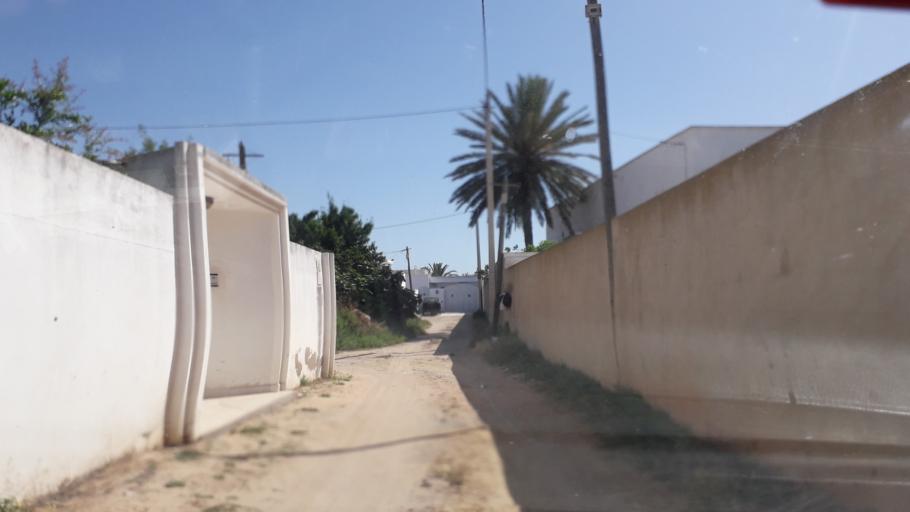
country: TN
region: Safaqis
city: Al Qarmadah
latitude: 34.8075
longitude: 10.7656
